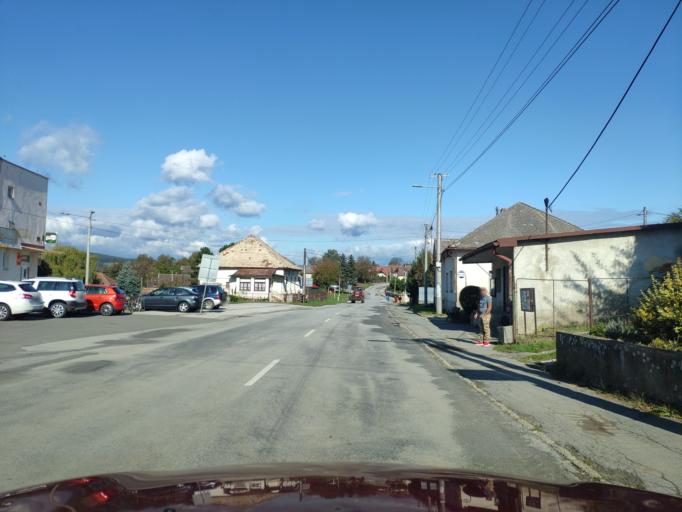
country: SK
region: Presovsky
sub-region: Okres Presov
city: Presov
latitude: 48.8722
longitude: 21.2712
